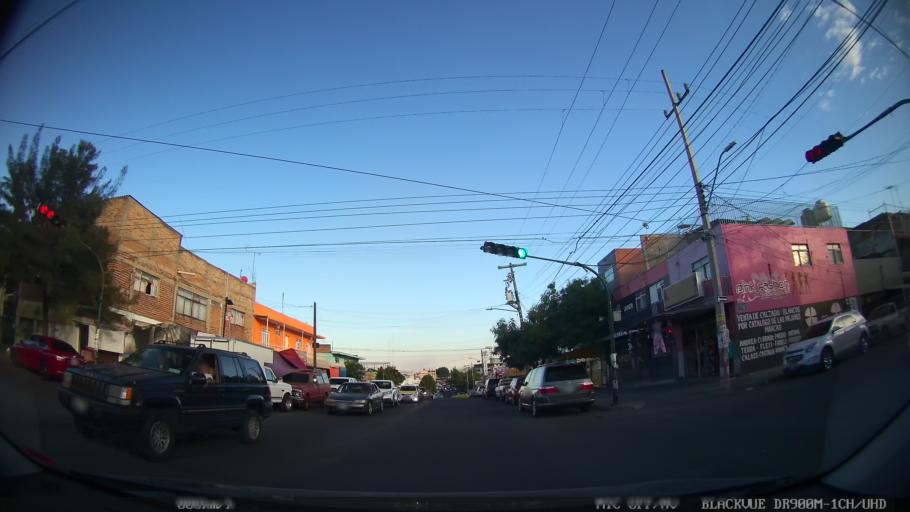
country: MX
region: Jalisco
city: Tlaquepaque
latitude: 20.7061
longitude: -103.2936
